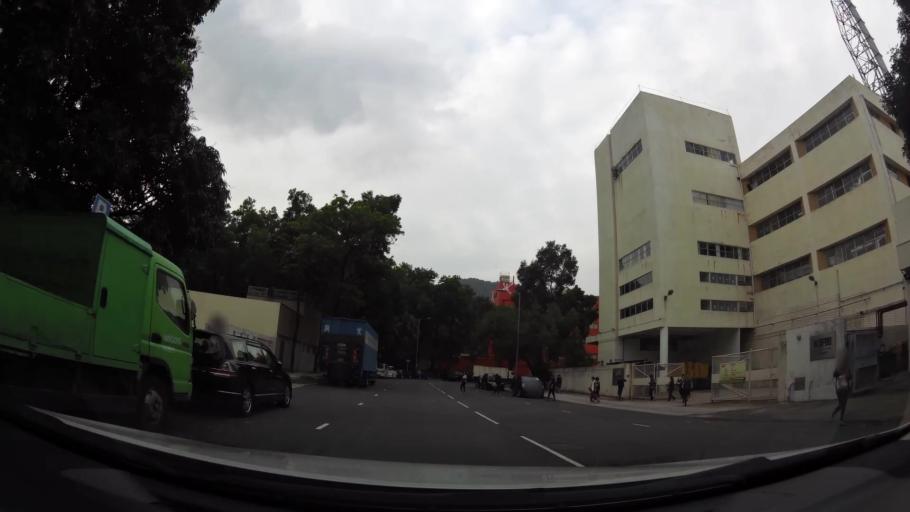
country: HK
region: Tai Po
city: Tai Po
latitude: 22.4605
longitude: 114.1847
